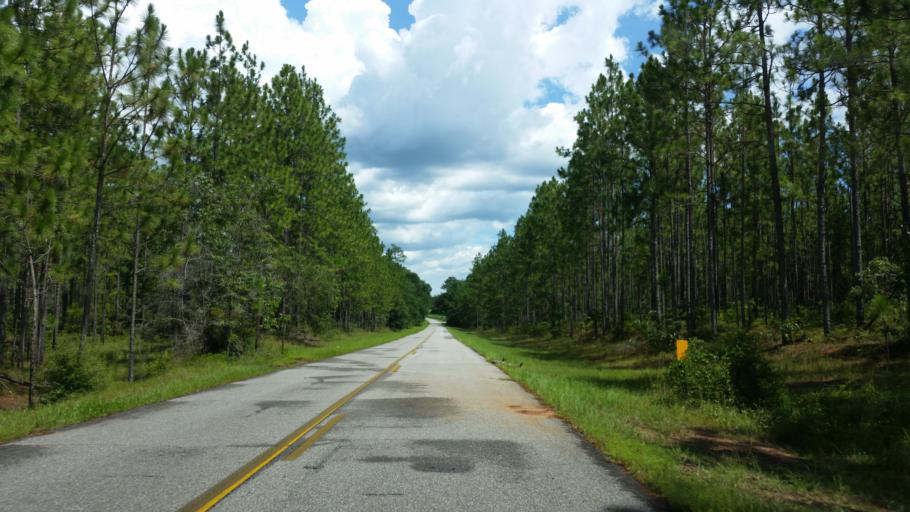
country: US
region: Florida
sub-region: Santa Rosa County
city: East Milton
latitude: 30.7381
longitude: -86.8196
